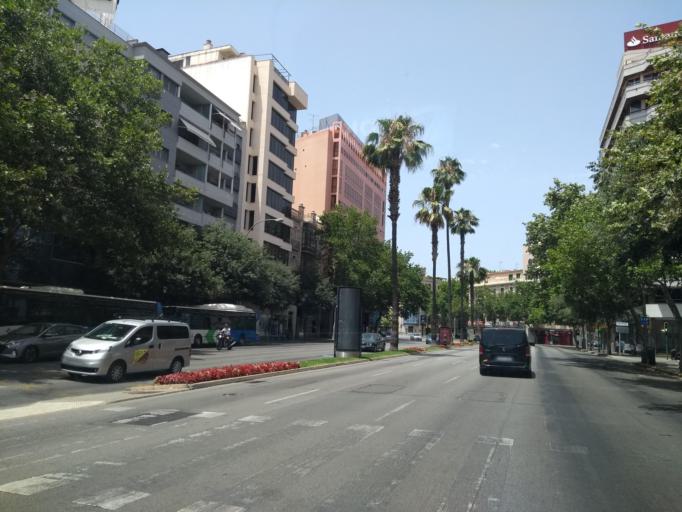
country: ES
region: Balearic Islands
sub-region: Illes Balears
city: Palma
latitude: 39.5764
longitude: 2.6535
